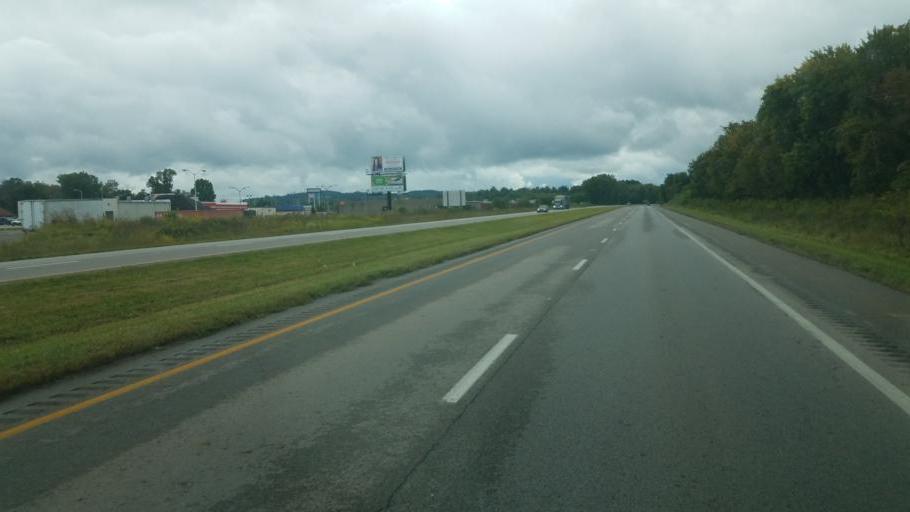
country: US
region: Ohio
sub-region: Scioto County
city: Wheelersburg
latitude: 38.7184
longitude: -82.8596
